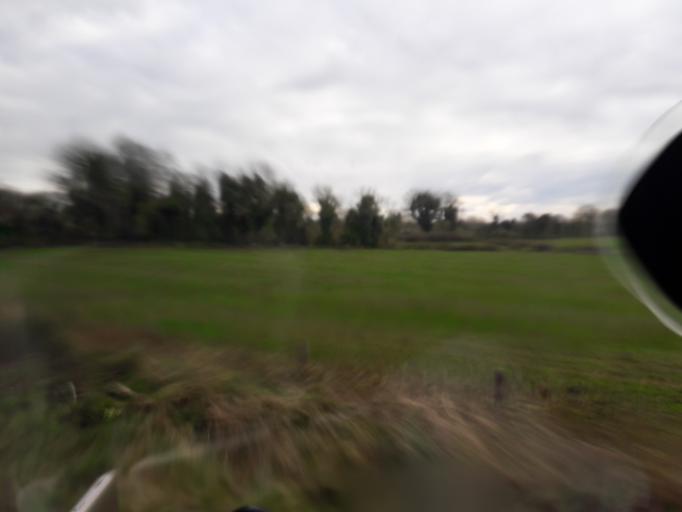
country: IE
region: Leinster
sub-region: An Longfort
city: Edgeworthstown
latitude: 53.6828
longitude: -7.5705
